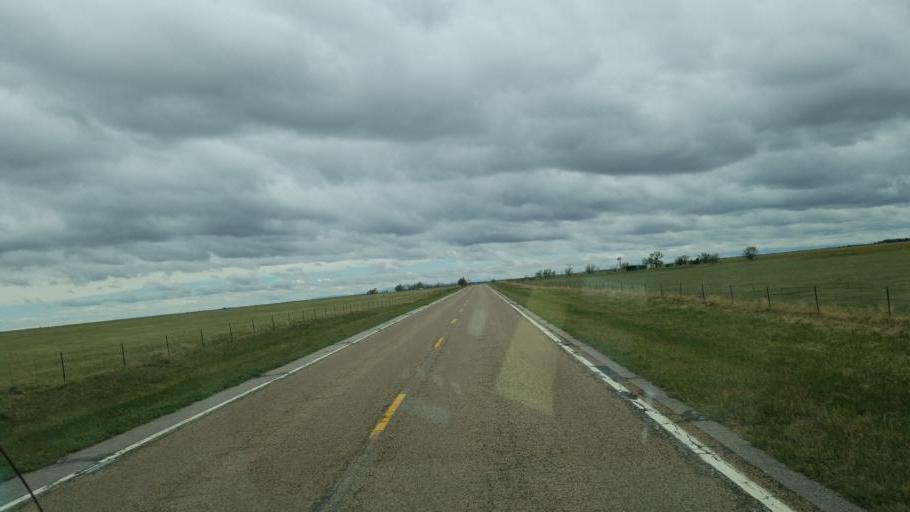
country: US
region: Colorado
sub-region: El Paso County
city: Ellicott
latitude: 38.8396
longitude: -103.9302
